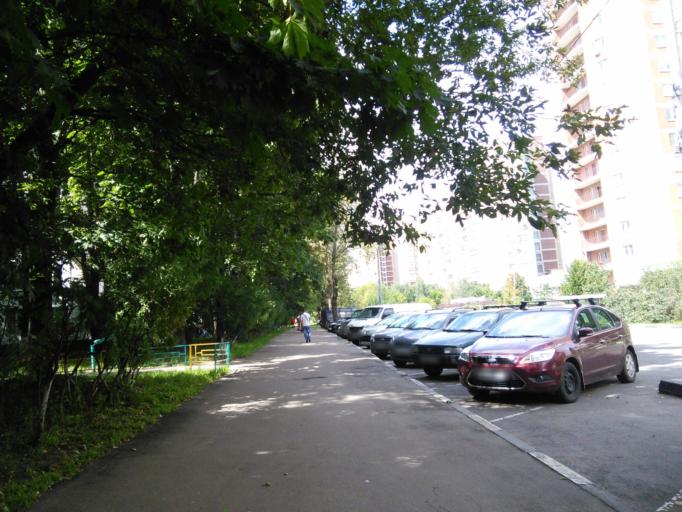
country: RU
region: Moscow
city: Tsaritsyno
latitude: 55.6368
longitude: 37.6673
